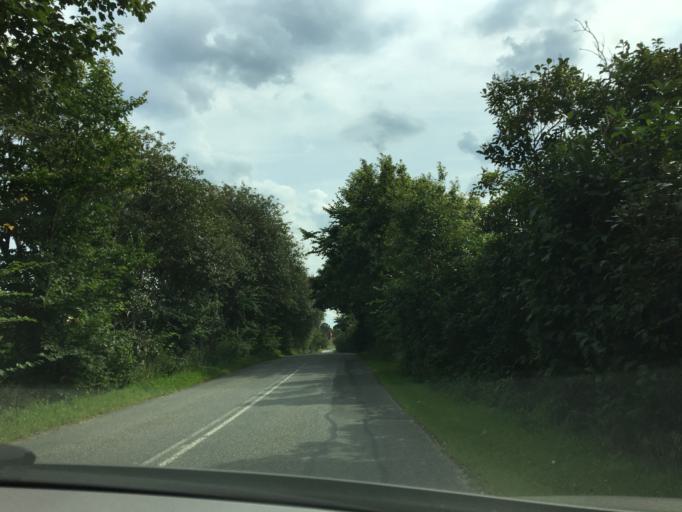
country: DK
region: Central Jutland
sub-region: Viborg Kommune
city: Stoholm
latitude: 56.4609
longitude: 9.1623
